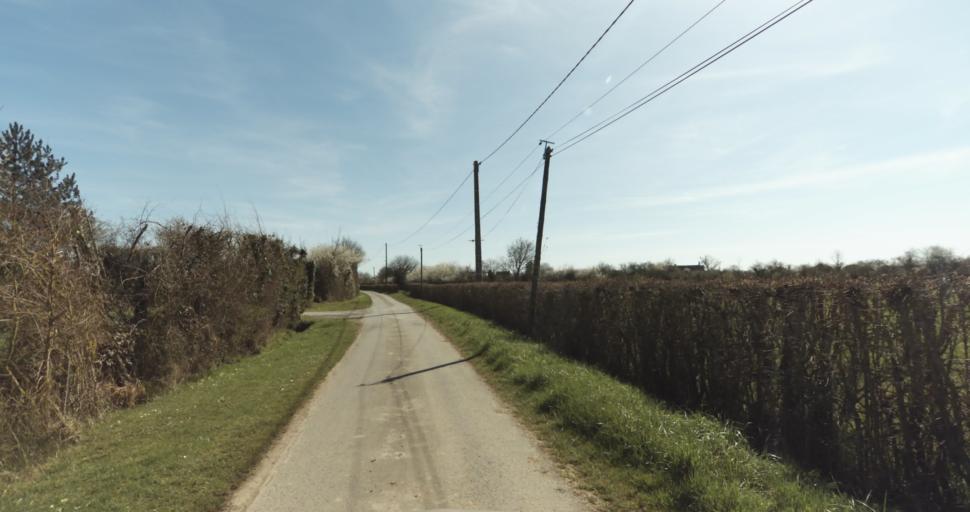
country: FR
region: Lower Normandy
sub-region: Departement du Calvados
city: Saint-Pierre-sur-Dives
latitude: 49.0531
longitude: -0.0343
